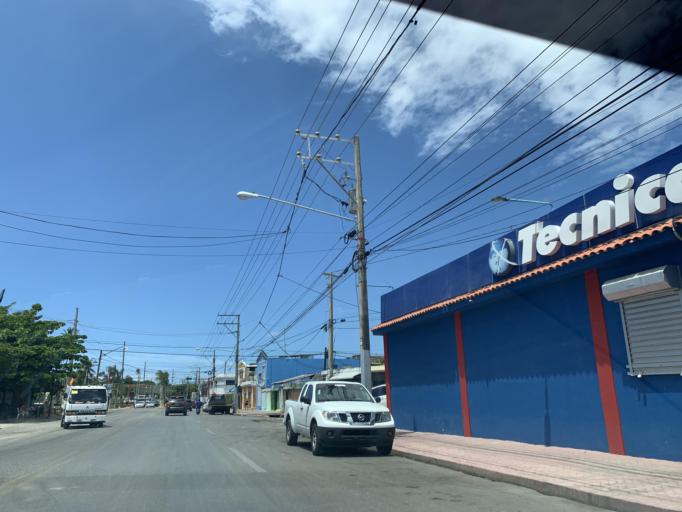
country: DO
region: Puerto Plata
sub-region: Puerto Plata
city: Puerto Plata
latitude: 19.7984
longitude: -70.6969
